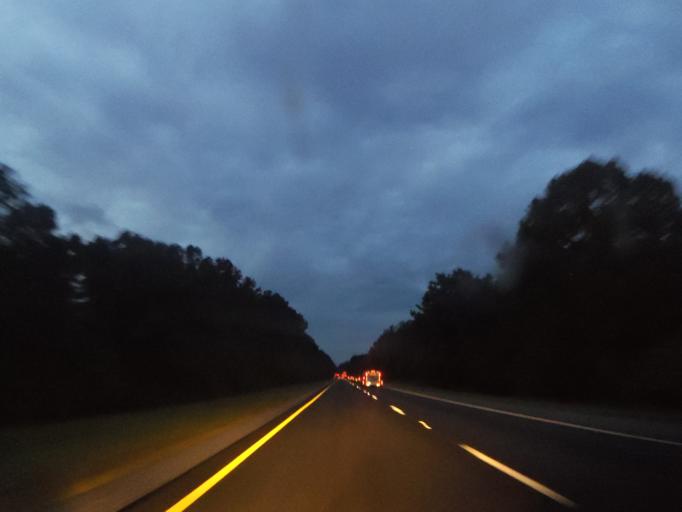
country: US
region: Alabama
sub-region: DeKalb County
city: Collinsville
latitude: 34.2916
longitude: -85.8676
